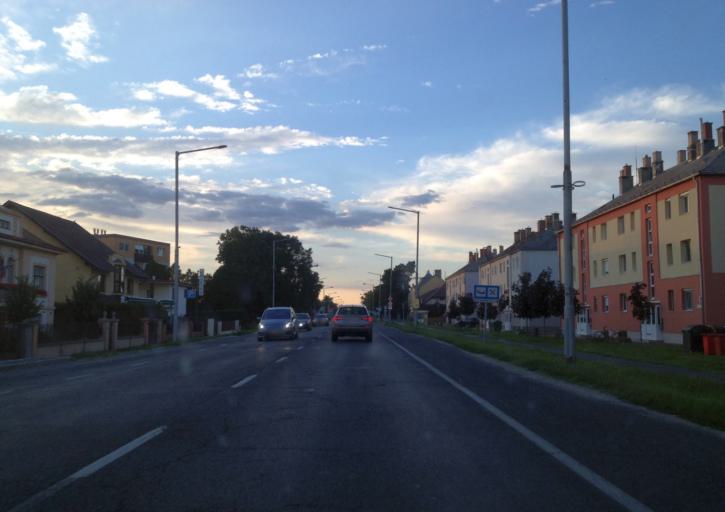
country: HU
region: Gyor-Moson-Sopron
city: Mosonmagyarovar
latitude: 47.8684
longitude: 17.2714
